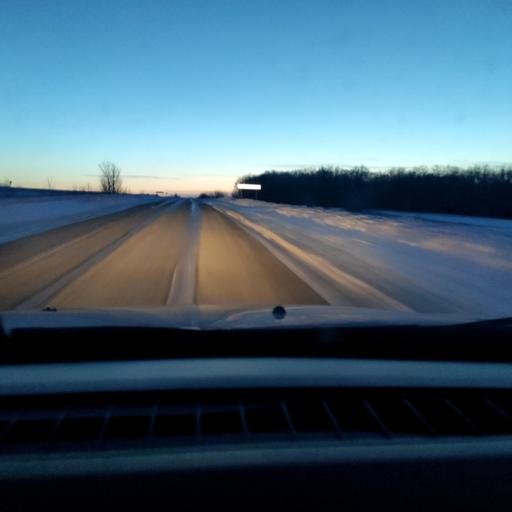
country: RU
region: Samara
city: Georgiyevka
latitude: 53.3145
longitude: 50.8460
